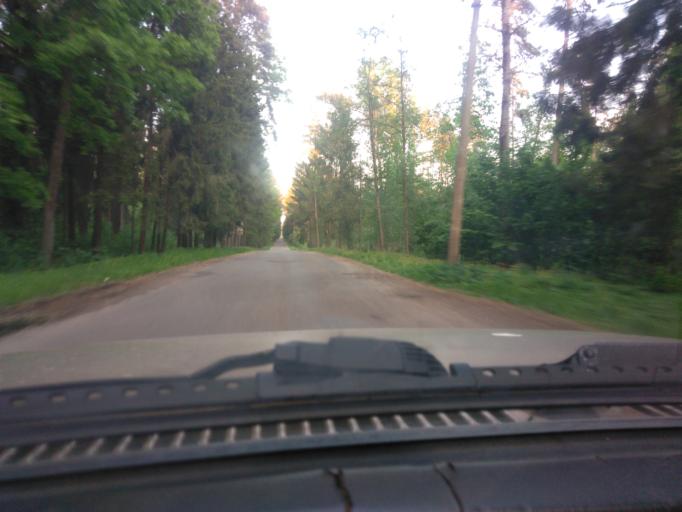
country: BY
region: Mogilev
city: Mahilyow
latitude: 53.9337
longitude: 30.2907
